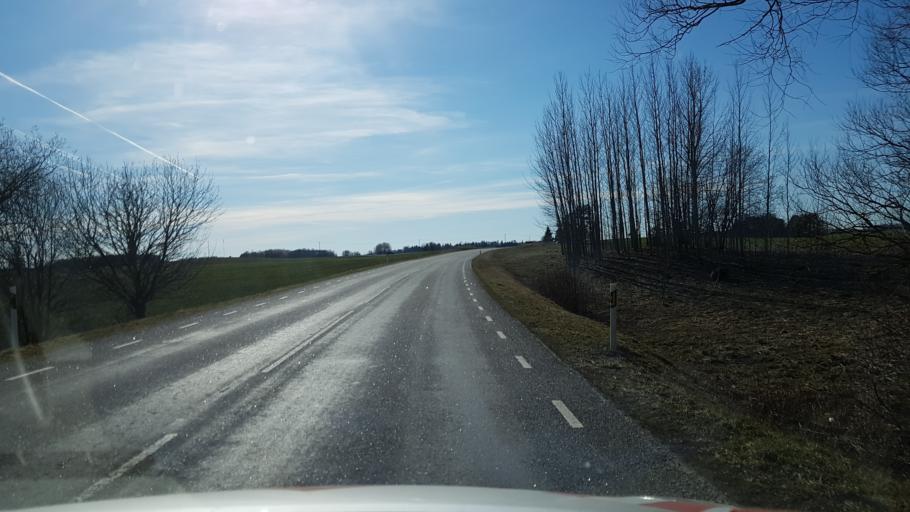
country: EE
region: Laeaene-Virumaa
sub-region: Vinni vald
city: Vinni
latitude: 59.3148
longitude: 26.4571
